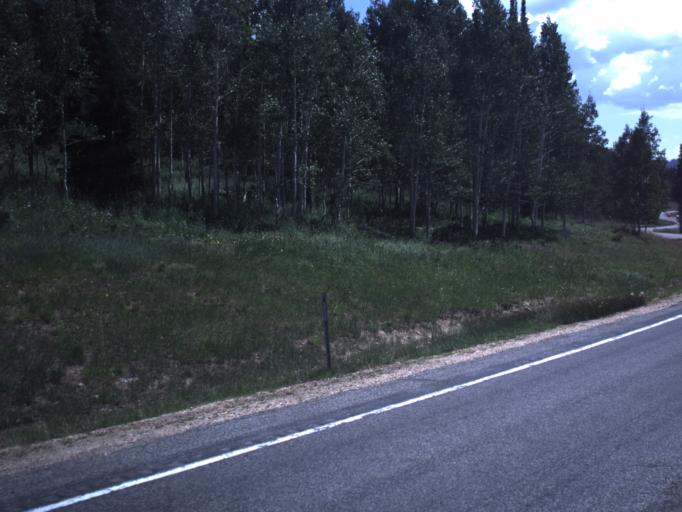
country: US
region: Utah
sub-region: Sanpete County
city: Fairview
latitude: 39.5966
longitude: -111.2703
